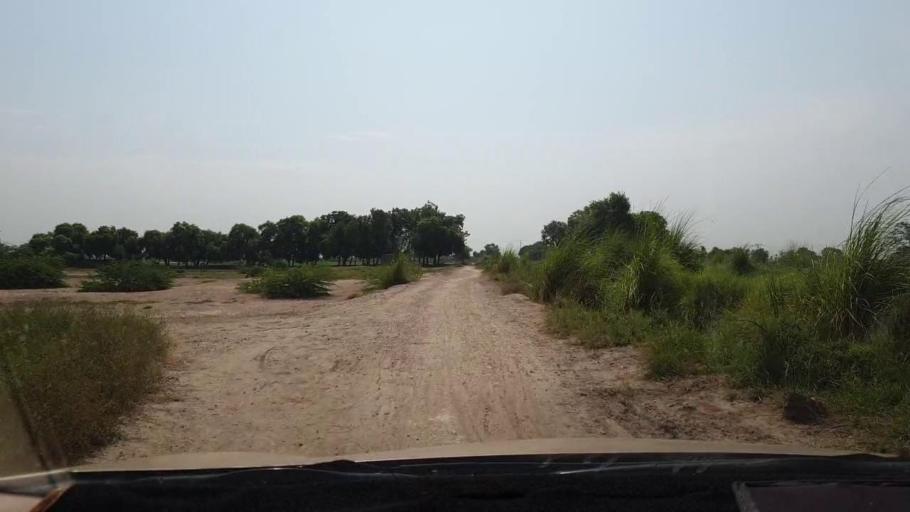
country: PK
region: Sindh
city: Larkana
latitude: 27.6364
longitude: 68.2429
